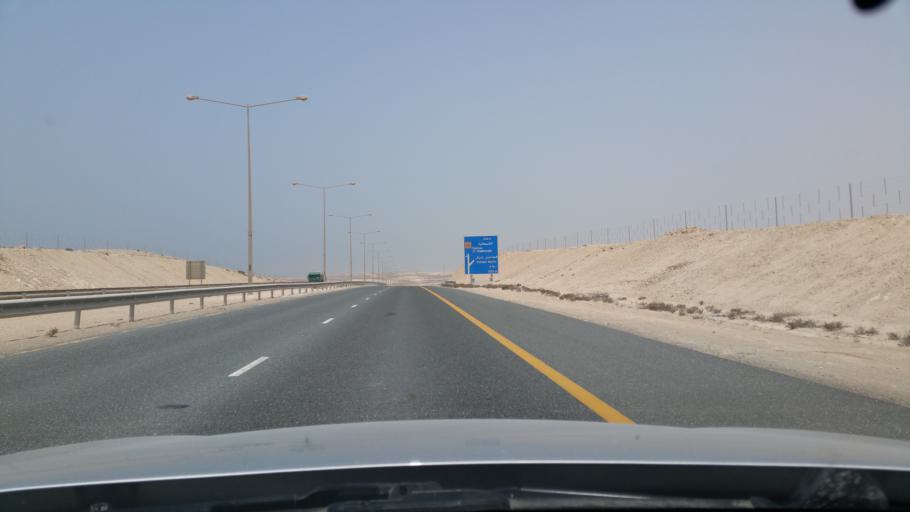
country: QA
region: Baladiyat ar Rayyan
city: Dukhan
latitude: 25.3275
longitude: 50.7865
